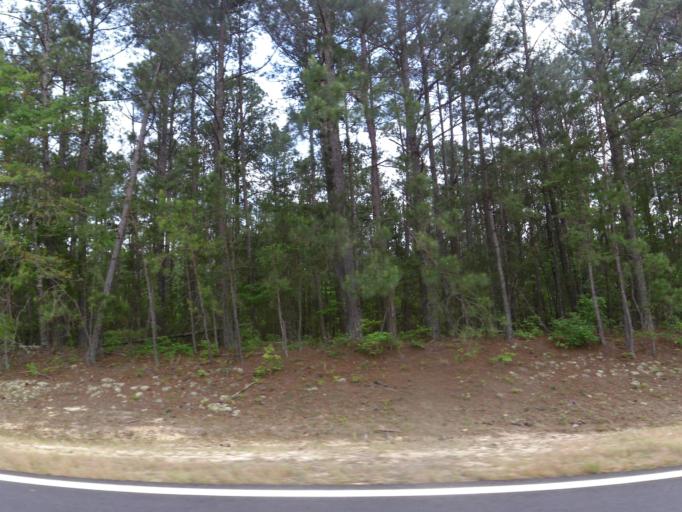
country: US
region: Georgia
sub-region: McDuffie County
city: Thomson
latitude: 33.5240
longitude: -82.4449
